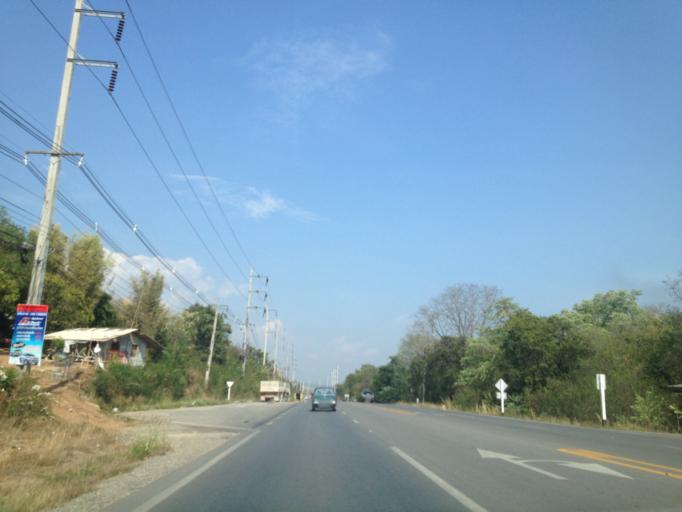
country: TH
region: Chiang Mai
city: Chom Thong
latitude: 18.3652
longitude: 98.6800
